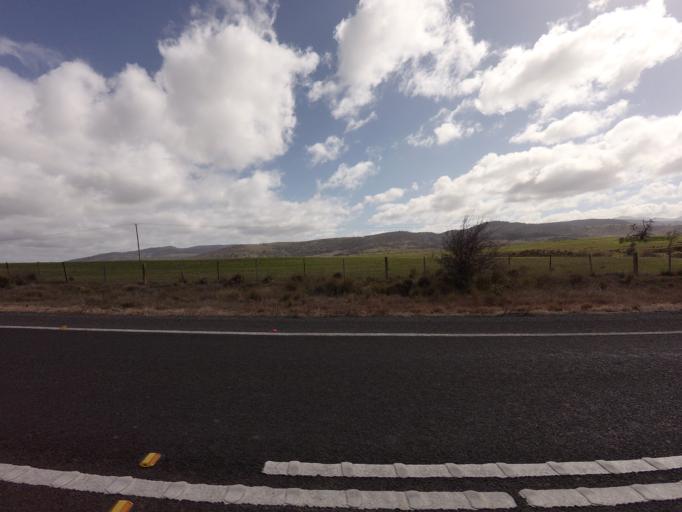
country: AU
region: Tasmania
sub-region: Northern Midlands
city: Evandale
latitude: -41.8058
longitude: 147.6810
